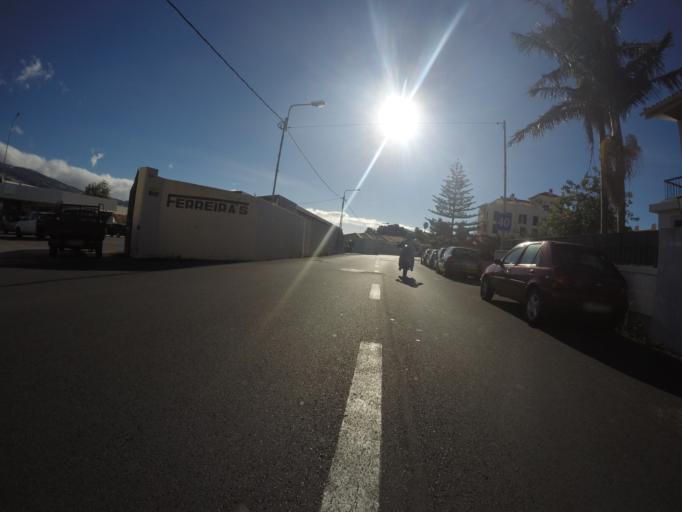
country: PT
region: Madeira
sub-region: Funchal
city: Nossa Senhora do Monte
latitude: 32.6542
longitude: -16.9245
